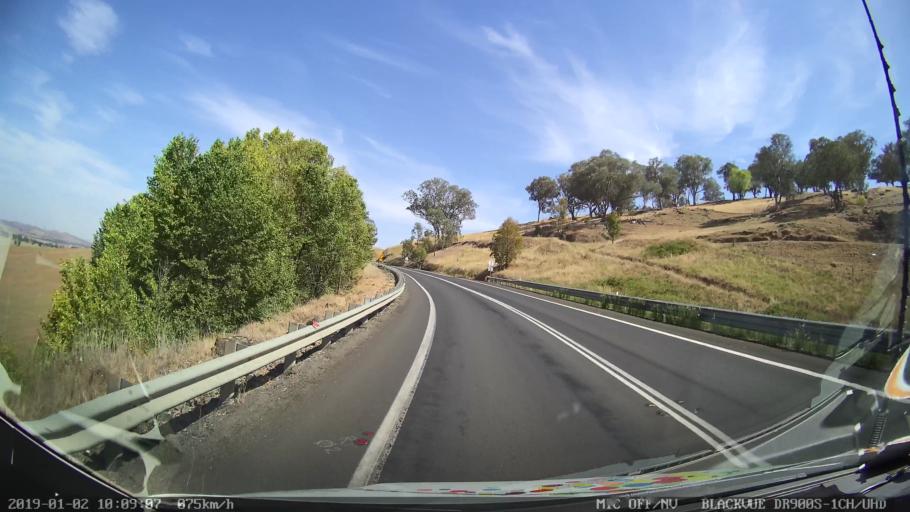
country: AU
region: New South Wales
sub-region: Gundagai
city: Gundagai
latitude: -35.1197
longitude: 148.1006
